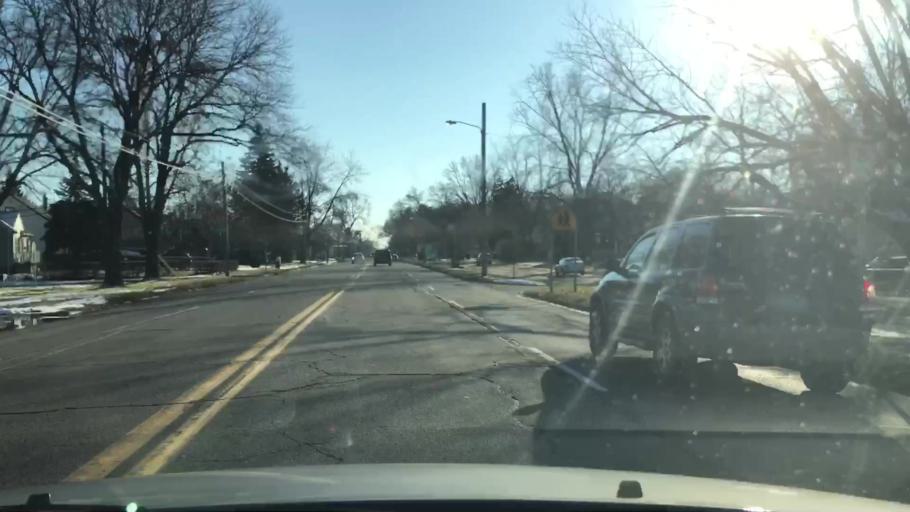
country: US
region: Michigan
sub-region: Oakland County
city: Clawson
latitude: 42.5151
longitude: -83.1405
